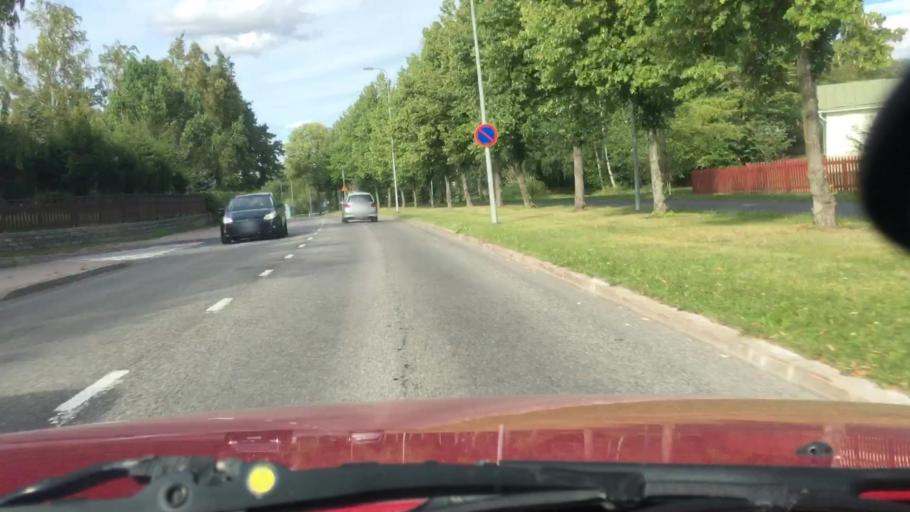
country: FI
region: Varsinais-Suomi
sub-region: Turku
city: Turku
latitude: 60.4567
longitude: 22.2451
